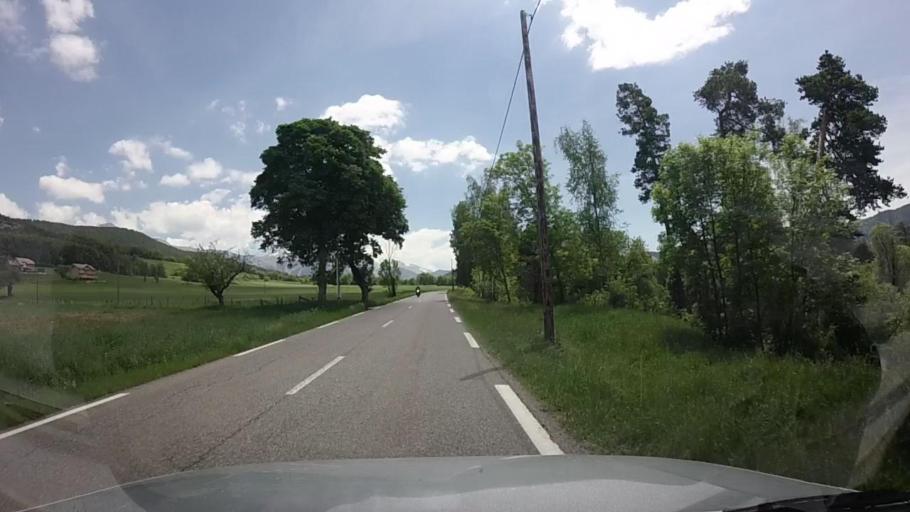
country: FR
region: Provence-Alpes-Cote d'Azur
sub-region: Departement des Alpes-de-Haute-Provence
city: Seyne-les-Alpes
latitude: 44.3626
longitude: 6.3273
